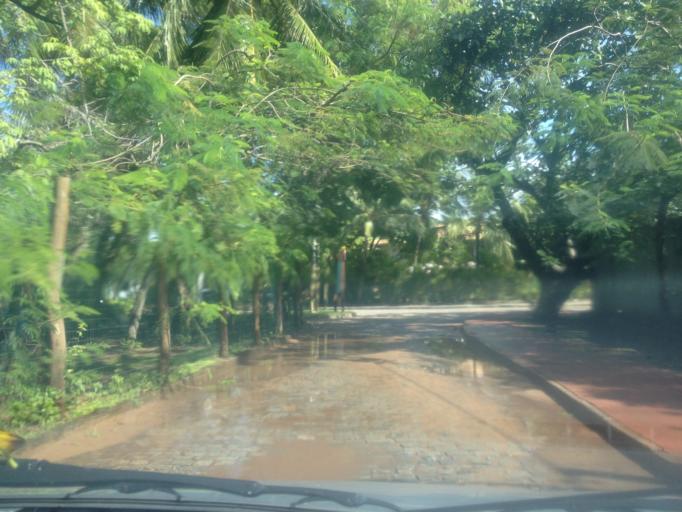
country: BR
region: Bahia
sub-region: Mata De Sao Joao
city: Mata de Sao Joao
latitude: -12.5757
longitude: -38.0040
